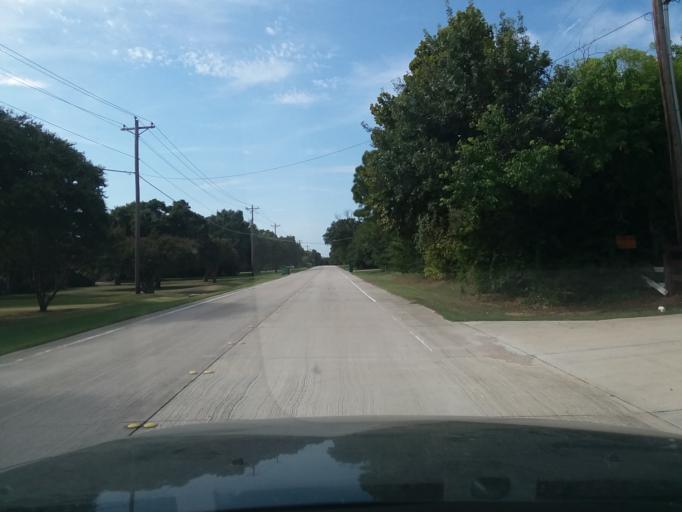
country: US
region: Texas
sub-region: Denton County
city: Double Oak
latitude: 33.0689
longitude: -97.1143
